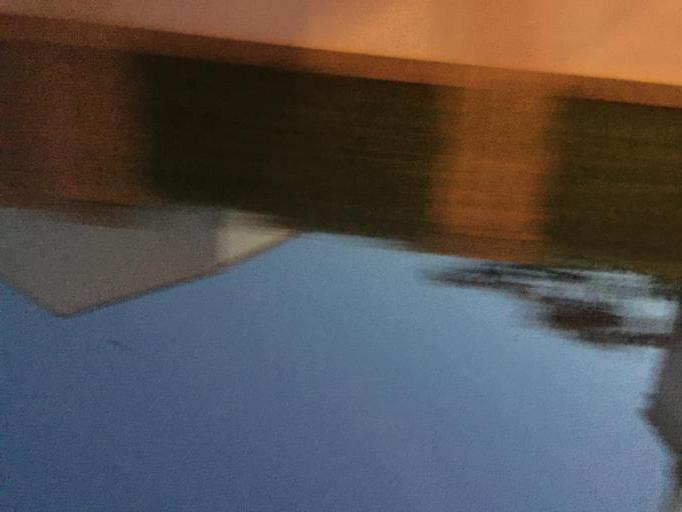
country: ES
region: Catalonia
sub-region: Provincia de Lleida
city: La Fuliola
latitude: 41.7067
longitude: 1.0340
